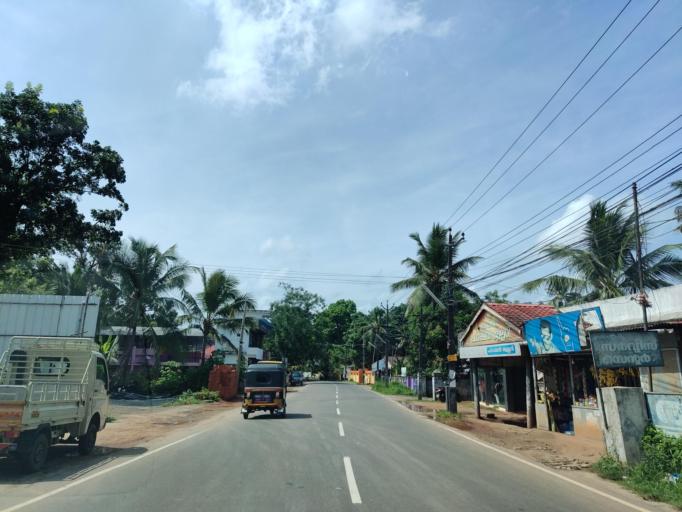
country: IN
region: Kerala
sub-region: Alappuzha
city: Mavelikara
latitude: 9.3031
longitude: 76.5340
